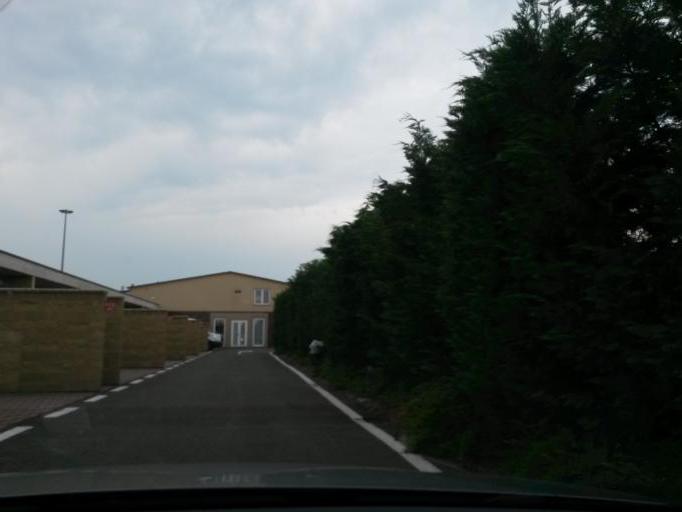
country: IT
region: Piedmont
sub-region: Provincia di Alessandria
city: Castelnuovo Scrivia
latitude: 44.9816
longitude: 8.9021
